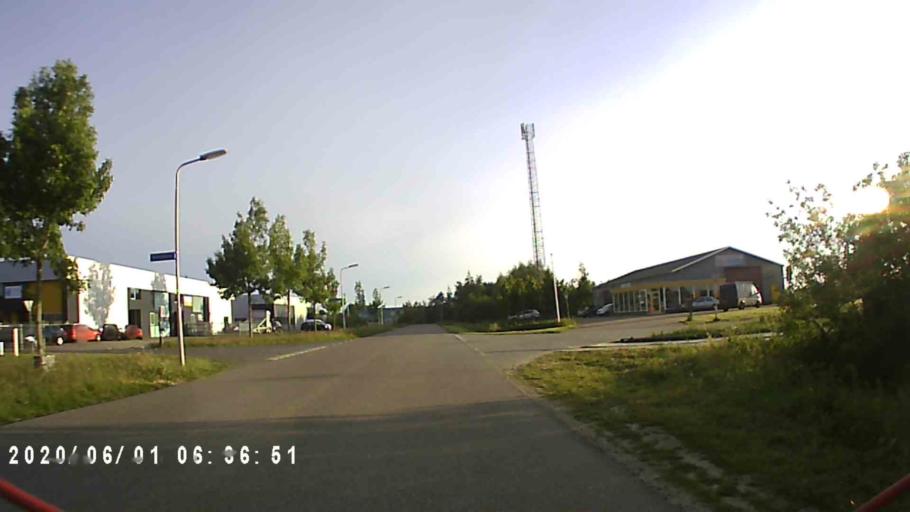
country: NL
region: Friesland
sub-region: Gemeente Kollumerland en Nieuwkruisland
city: Kollum
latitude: 53.2830
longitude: 6.1609
